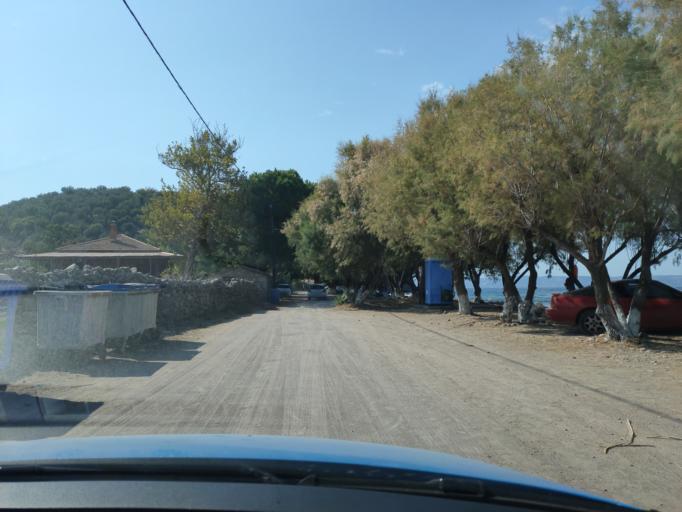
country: GR
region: North Aegean
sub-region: Nomos Lesvou
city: Mantamados
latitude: 39.3741
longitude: 26.3113
